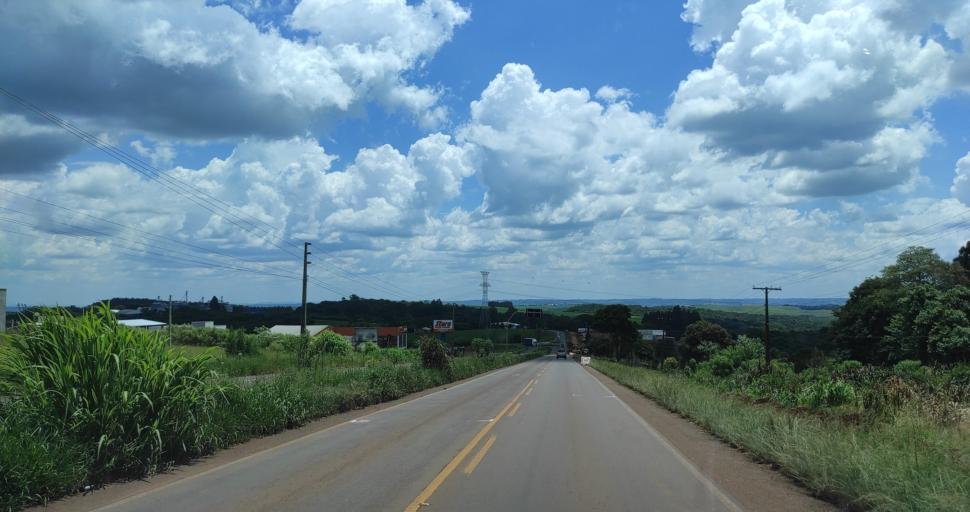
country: BR
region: Santa Catarina
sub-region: Xanxere
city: Xanxere
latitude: -26.8475
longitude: -52.4070
